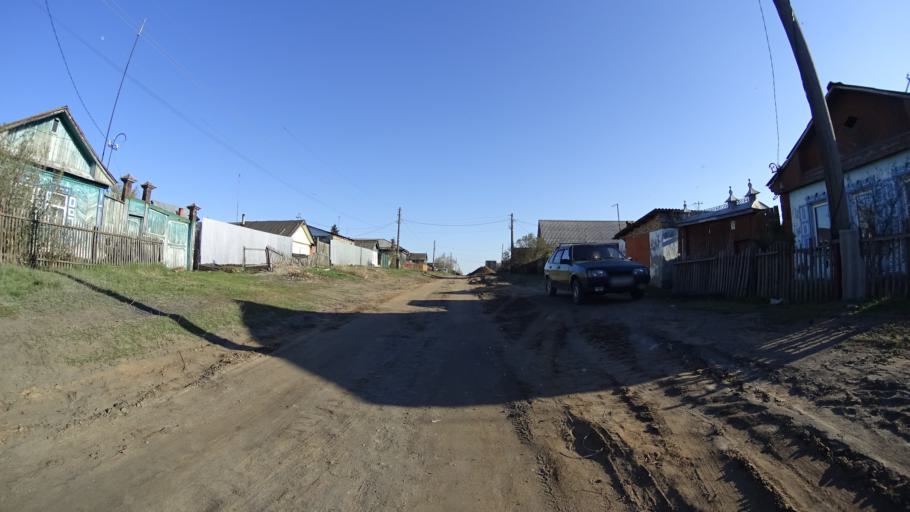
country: RU
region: Chelyabinsk
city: Troitsk
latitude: 54.0909
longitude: 61.5941
